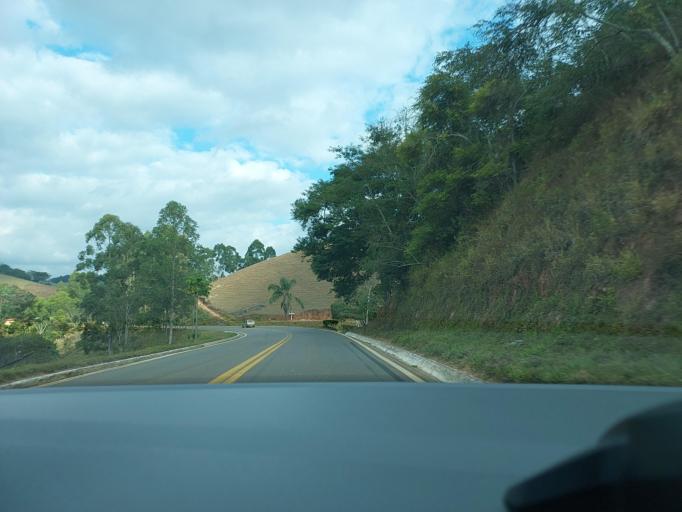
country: BR
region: Minas Gerais
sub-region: Visconde Do Rio Branco
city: Visconde do Rio Branco
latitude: -20.9163
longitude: -42.6400
